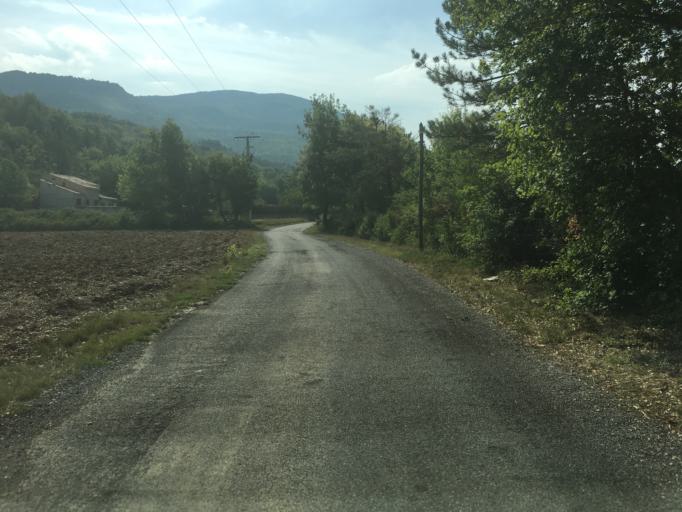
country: FR
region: Provence-Alpes-Cote d'Azur
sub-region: Departement des Alpes-de-Haute-Provence
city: Mallemoisson
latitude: 43.9364
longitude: 6.1860
